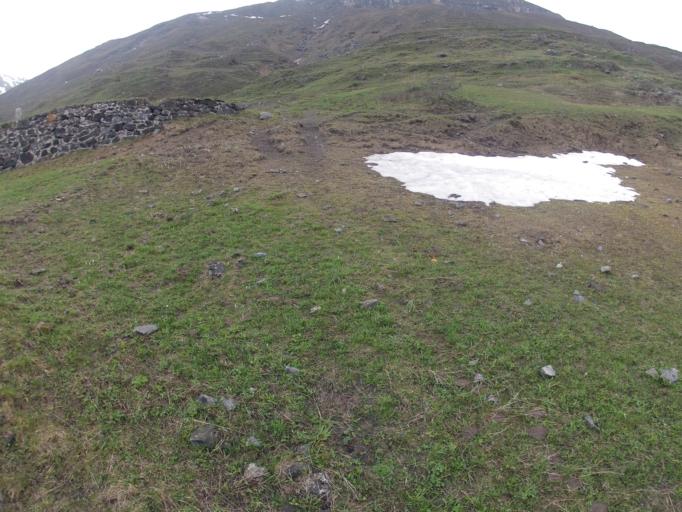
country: IT
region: Piedmont
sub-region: Provincia di Cuneo
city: Crissolo
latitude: 44.7011
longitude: 7.1189
